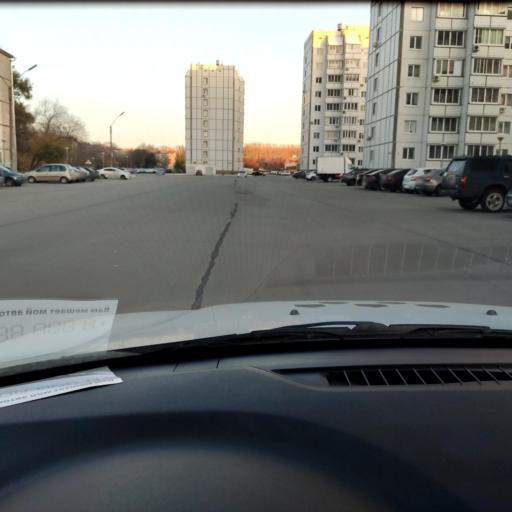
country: RU
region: Samara
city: Tol'yatti
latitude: 53.5205
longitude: 49.4197
